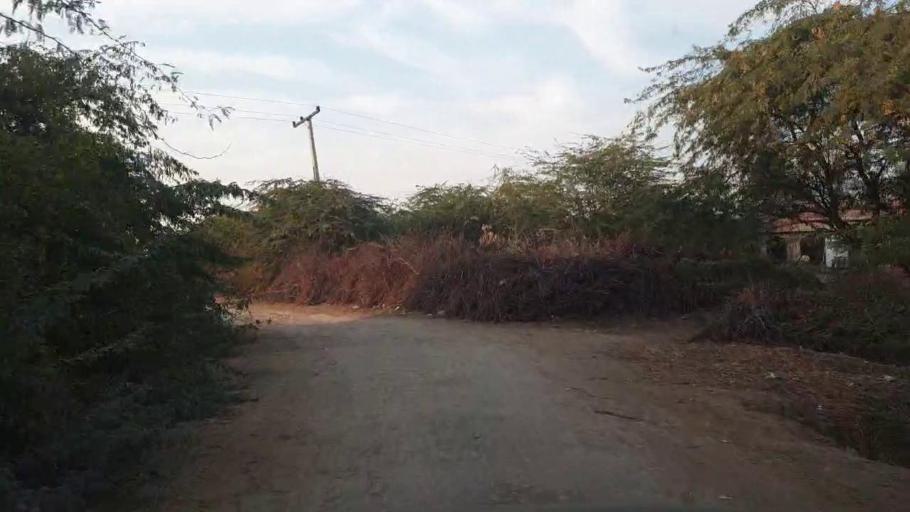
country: PK
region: Sindh
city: Shahpur Chakar
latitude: 26.1836
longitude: 68.6179
